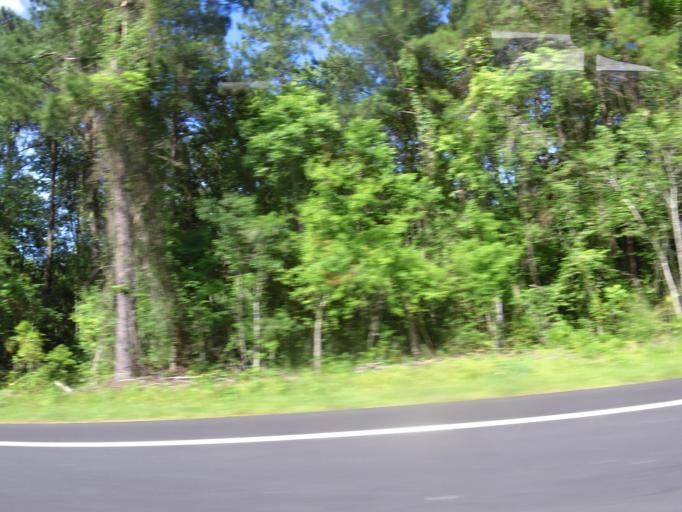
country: US
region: Florida
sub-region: Nassau County
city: Hilliard
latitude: 30.6668
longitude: -81.9043
